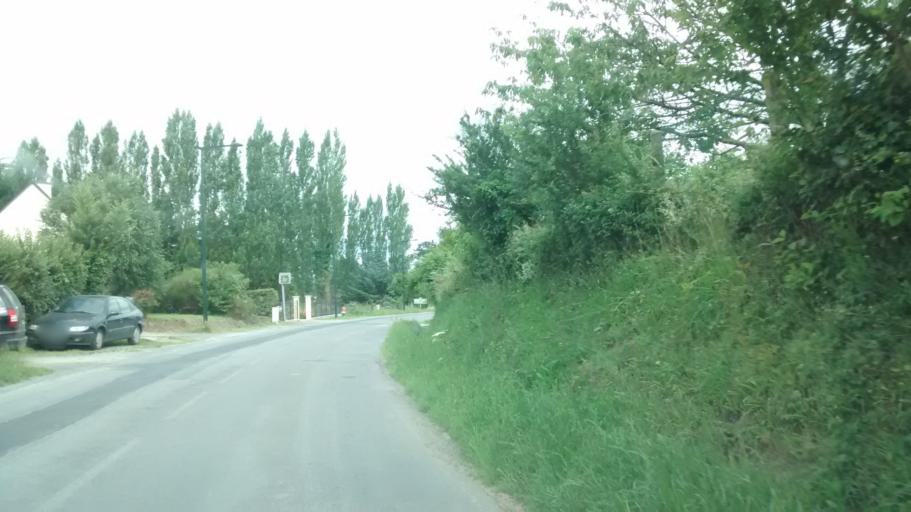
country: FR
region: Brittany
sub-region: Departement d'Ille-et-Vilaine
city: Saint-Meloir-des-Ondes
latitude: 48.6411
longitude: -1.9124
